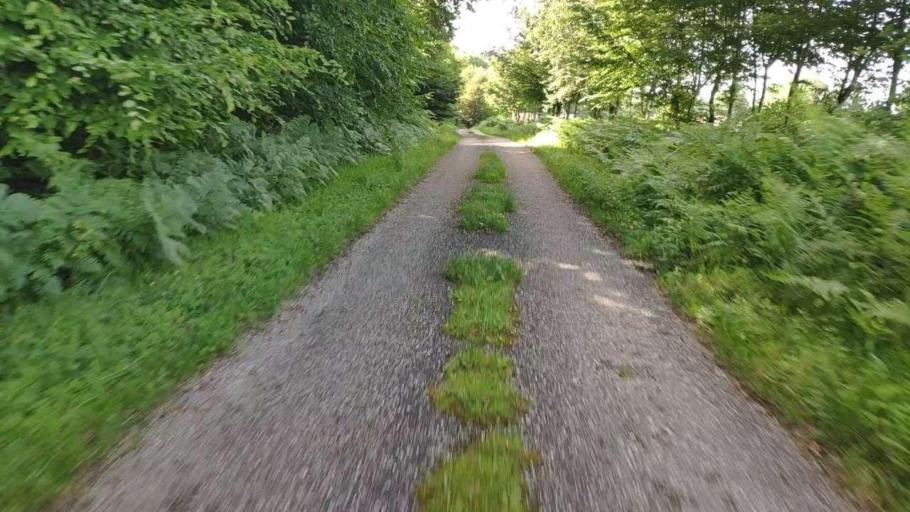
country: FR
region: Franche-Comte
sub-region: Departement du Jura
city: Bletterans
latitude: 46.8037
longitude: 5.4994
